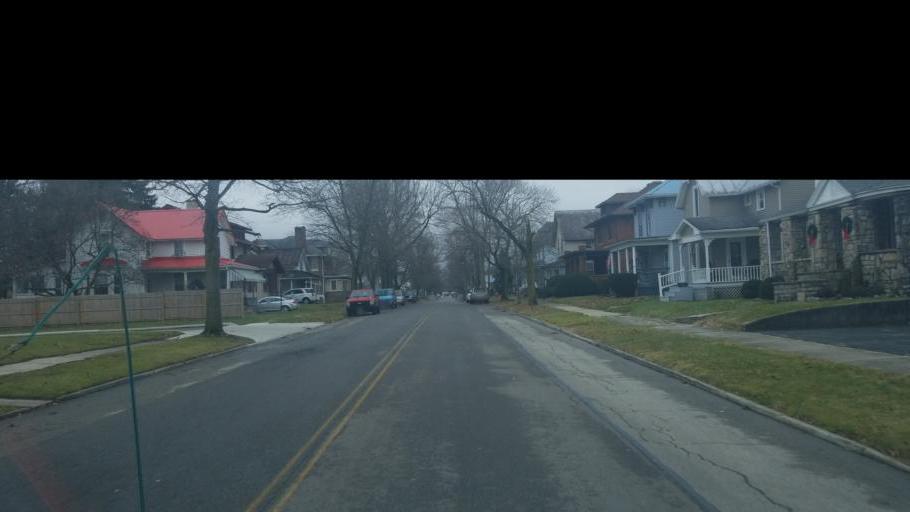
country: US
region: Ohio
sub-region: Crawford County
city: Bucyrus
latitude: 40.8047
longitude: -82.9771
